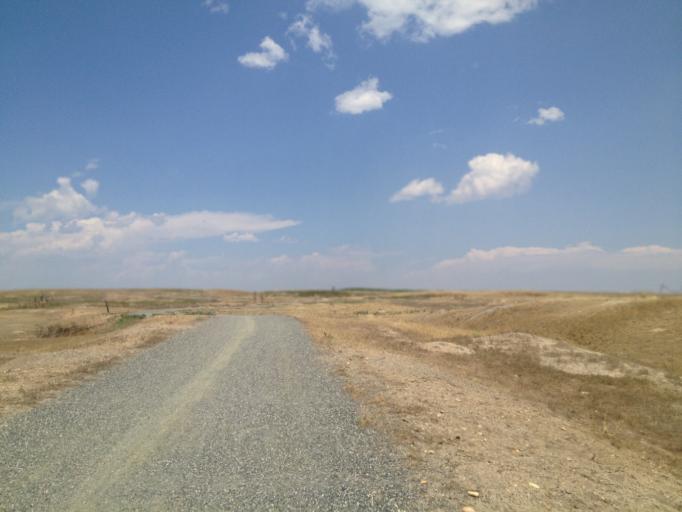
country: US
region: Colorado
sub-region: Boulder County
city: Lafayette
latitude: 39.9934
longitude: -105.0555
